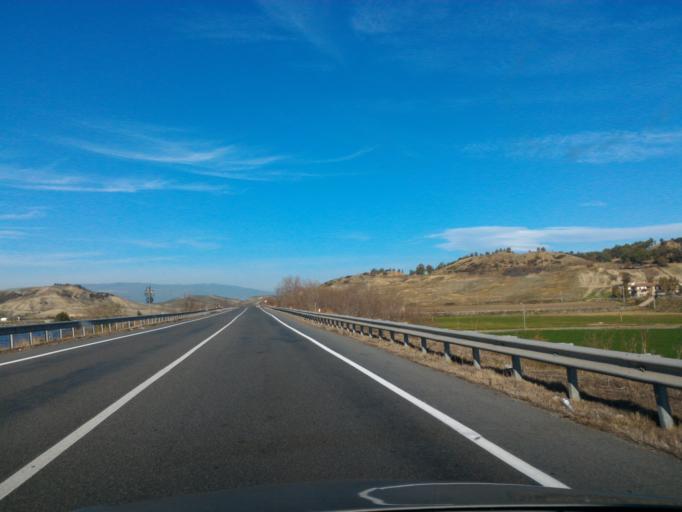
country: IT
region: Calabria
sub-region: Provincia di Crotone
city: Le Castella
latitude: 38.9424
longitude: 16.9565
